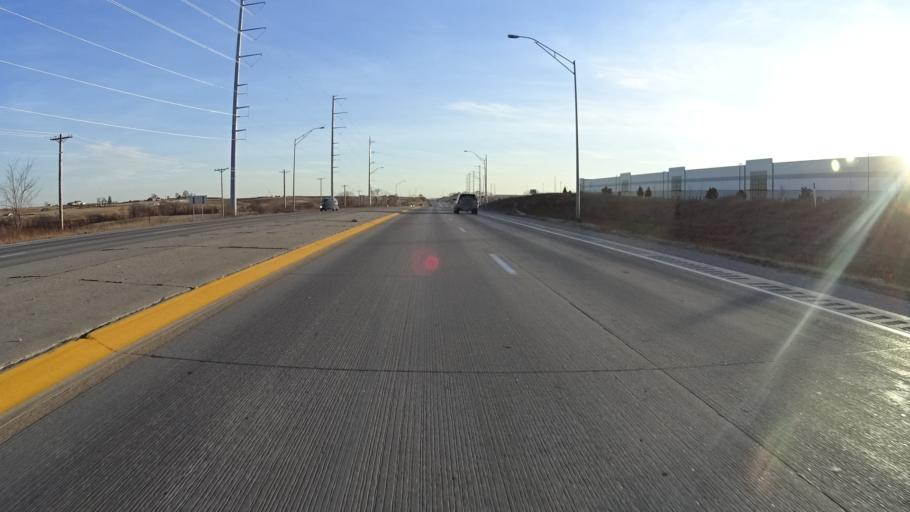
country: US
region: Nebraska
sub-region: Sarpy County
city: Chalco
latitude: 41.1442
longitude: -96.1390
